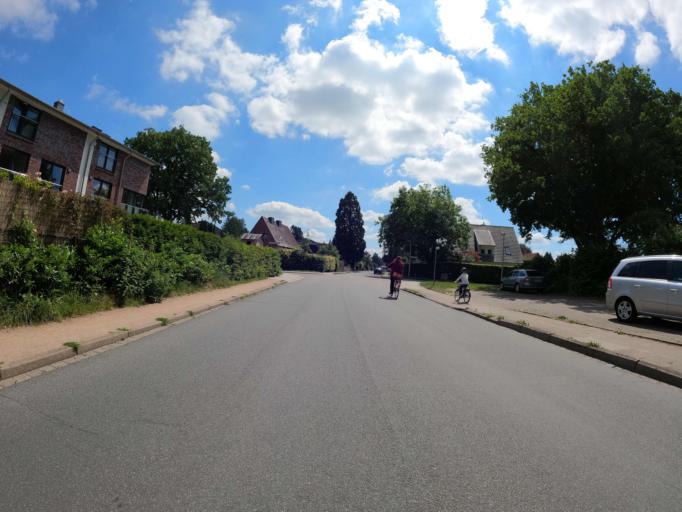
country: DE
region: Schleswig-Holstein
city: Wentorf bei Hamburg
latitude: 53.4943
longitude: 10.2654
